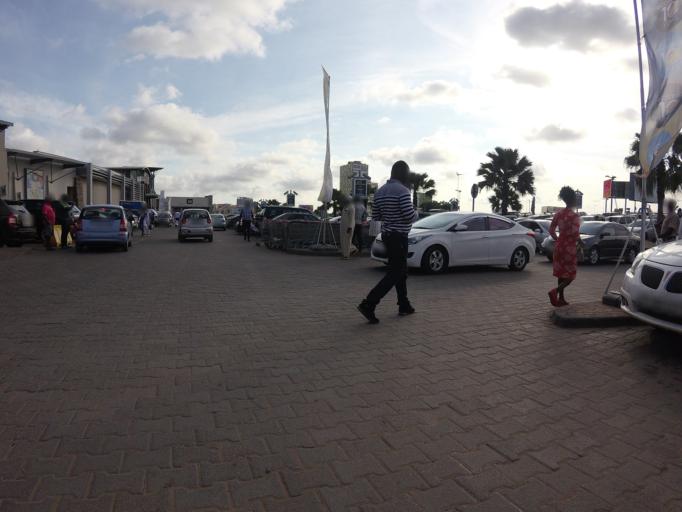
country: GH
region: Greater Accra
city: Medina Estates
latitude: 5.6230
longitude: -0.1733
